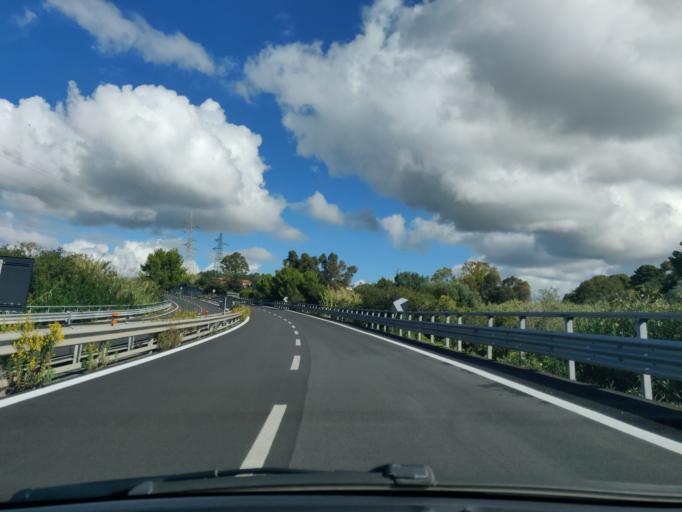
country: IT
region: Latium
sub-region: Citta metropolitana di Roma Capitale
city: Civitavecchia
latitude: 42.1075
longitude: 11.7921
